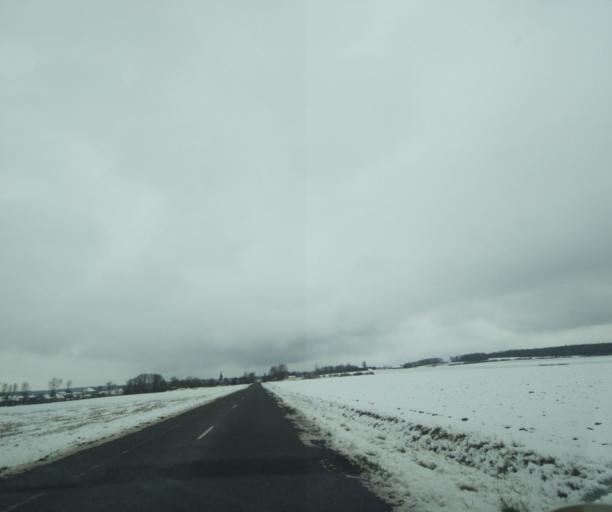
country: FR
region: Champagne-Ardenne
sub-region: Departement de la Haute-Marne
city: Laneuville-a-Remy
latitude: 48.4148
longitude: 4.8299
